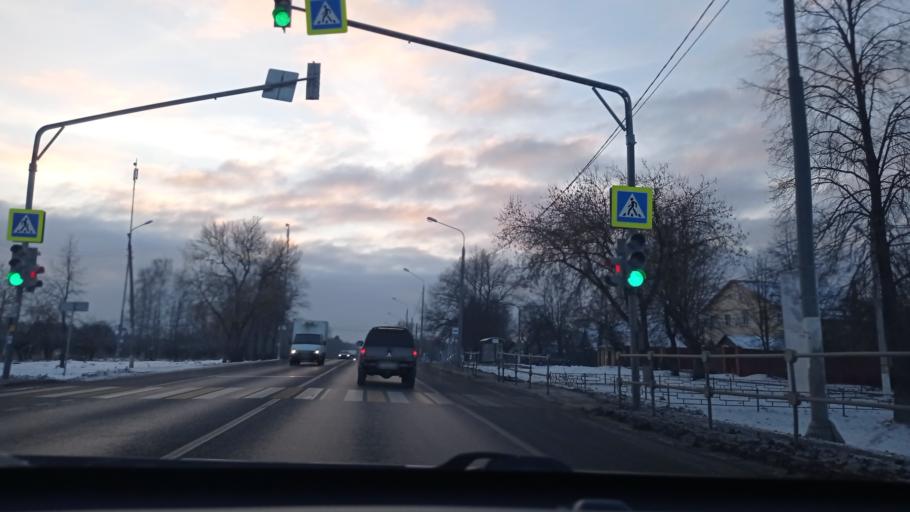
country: RU
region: Moskovskaya
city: Selyatino
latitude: 55.2618
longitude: 37.1028
